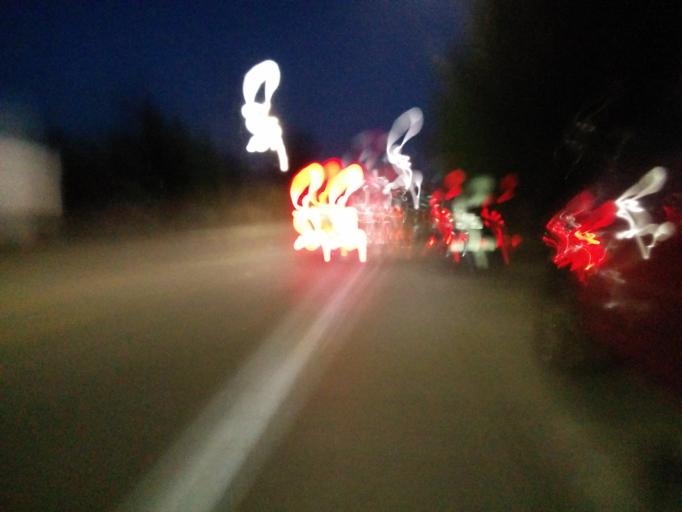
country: US
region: Washington
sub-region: King County
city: Seattle
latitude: 47.6649
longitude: -122.3663
